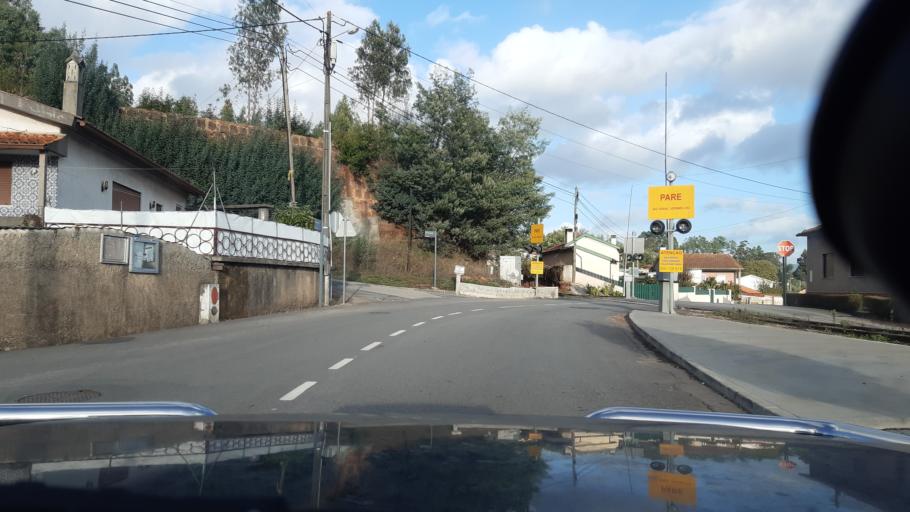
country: PT
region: Aveiro
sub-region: Agueda
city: Agueda
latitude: 40.5752
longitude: -8.4662
